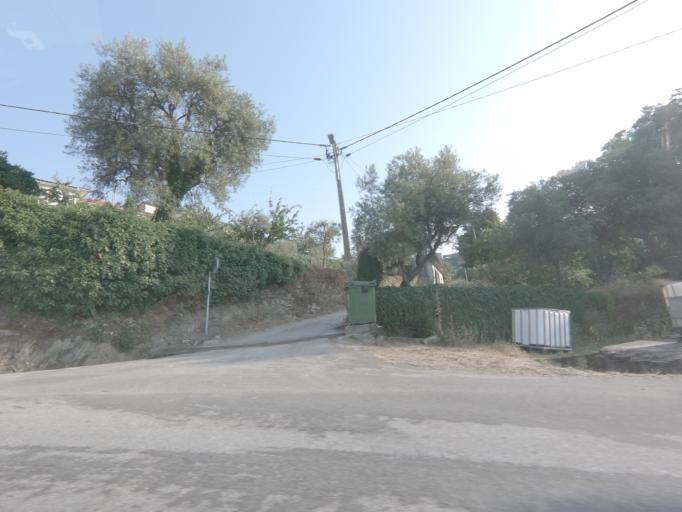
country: PT
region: Viseu
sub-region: Tabuaco
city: Tabuaco
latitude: 41.1457
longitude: -7.6106
